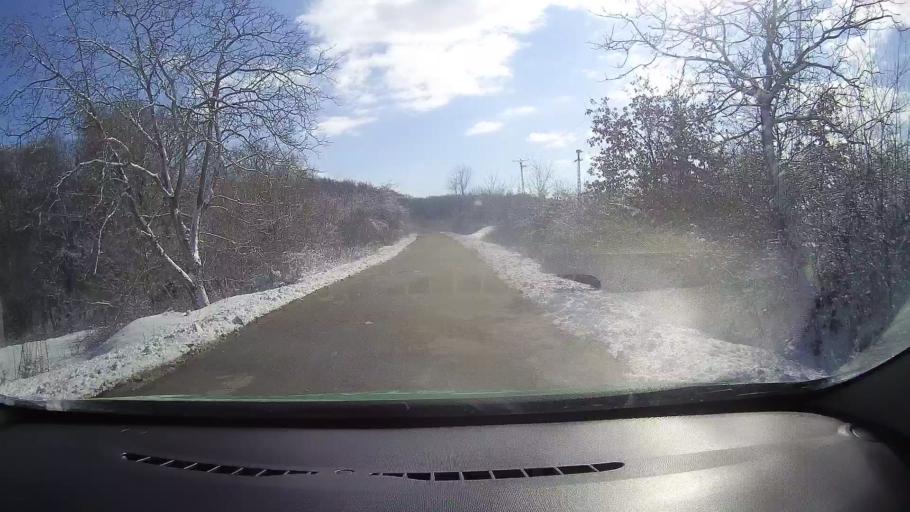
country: RO
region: Sibiu
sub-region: Comuna Mihaileni
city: Mihaileni
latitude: 46.0018
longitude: 24.4268
